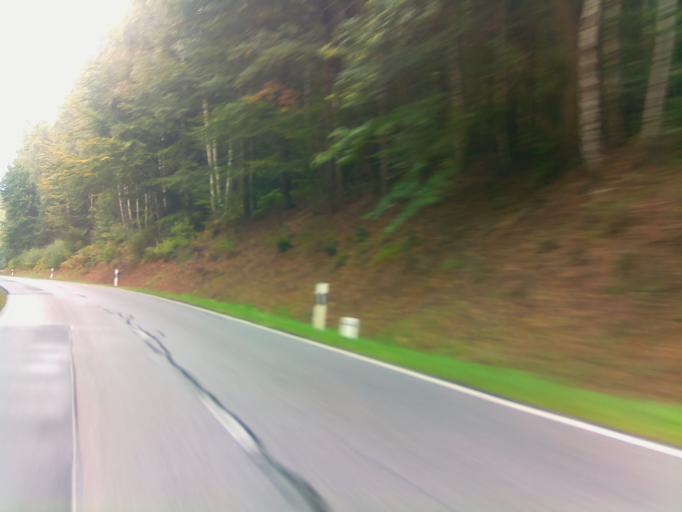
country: DE
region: Hesse
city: Hochst im Odenwald
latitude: 49.7804
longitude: 8.9758
